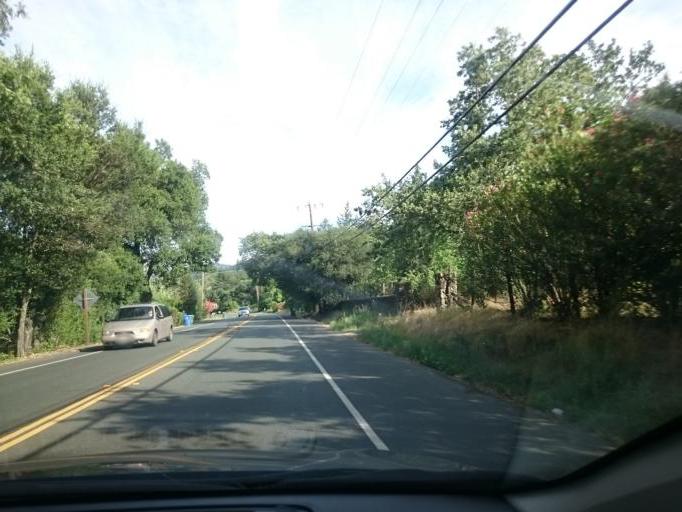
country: US
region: California
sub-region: Napa County
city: Calistoga
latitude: 38.5877
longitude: -122.6061
